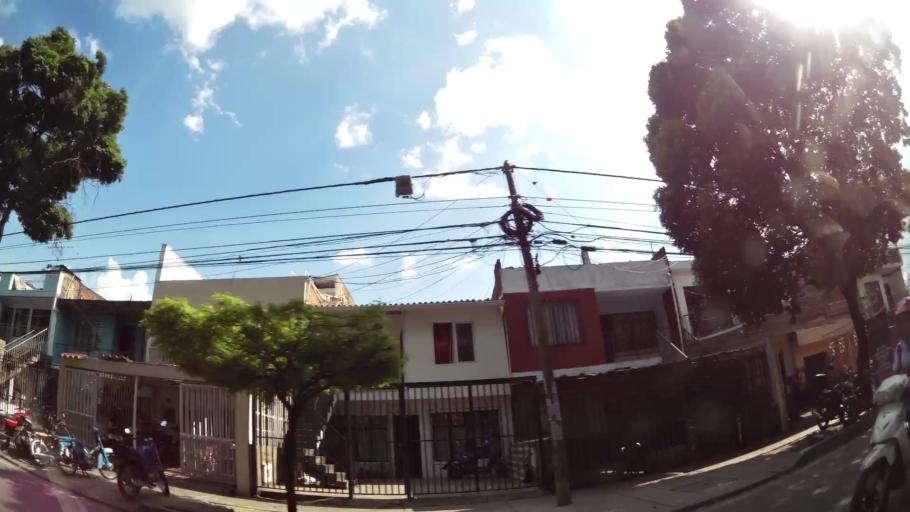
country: CO
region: Valle del Cauca
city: Cali
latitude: 3.4199
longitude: -76.5099
